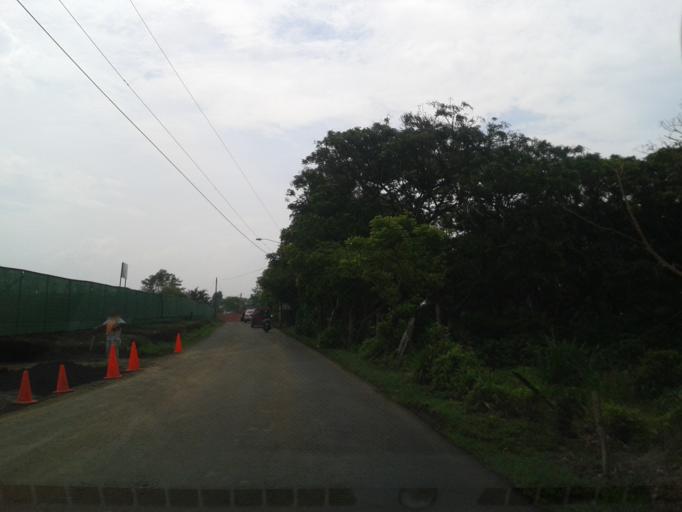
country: CR
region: Heredia
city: San Pablo
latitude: 9.9852
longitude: -84.1056
